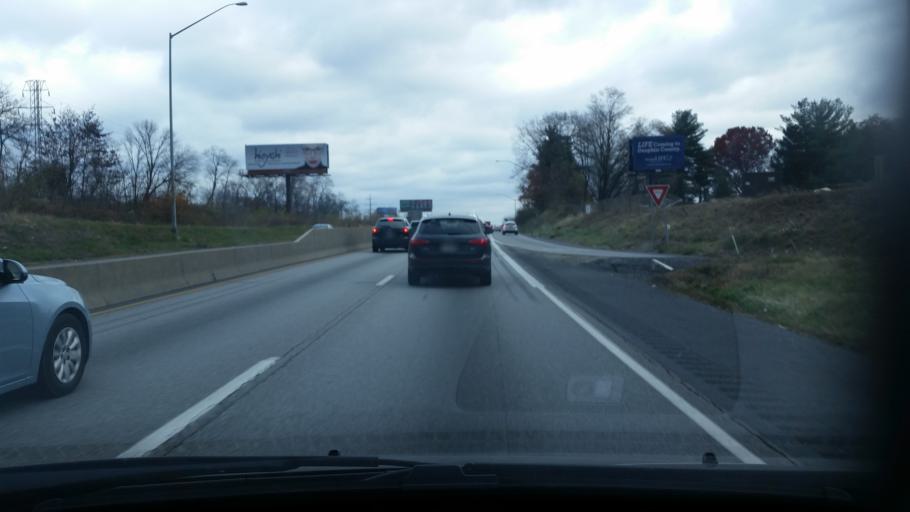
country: US
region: Pennsylvania
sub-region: Dauphin County
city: Penbrook
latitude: 40.2570
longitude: -76.8545
